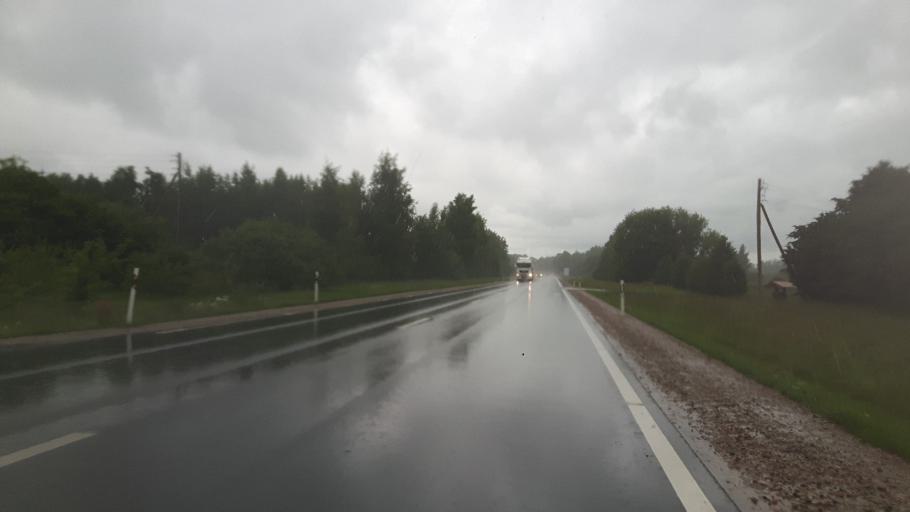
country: LV
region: Nica
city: Nica
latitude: 56.3391
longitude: 21.0700
